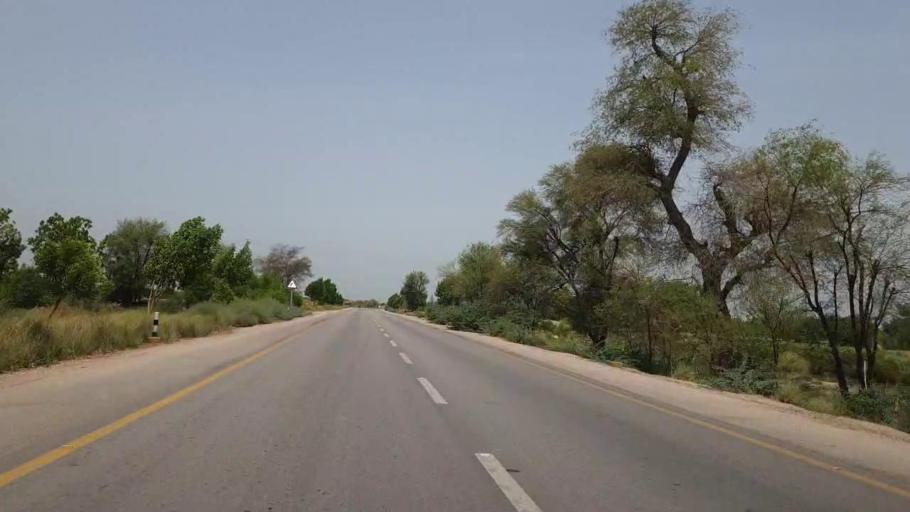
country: PK
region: Sindh
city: Nawabshah
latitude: 26.2136
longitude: 68.5117
